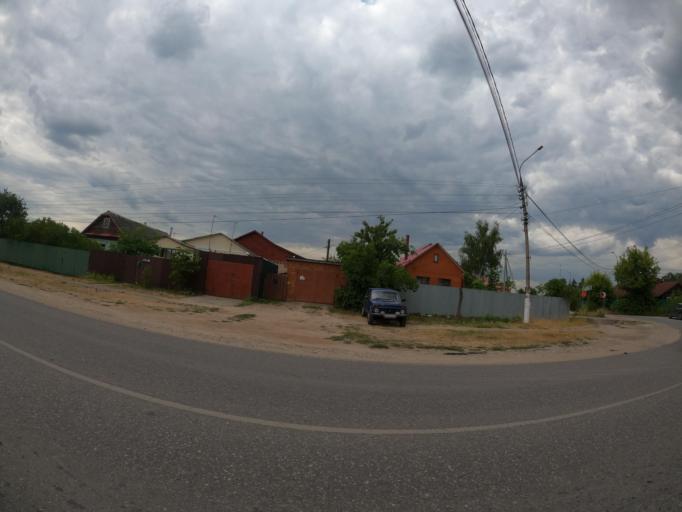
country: RU
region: Moskovskaya
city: Ramenskoye
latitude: 55.5437
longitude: 38.2350
